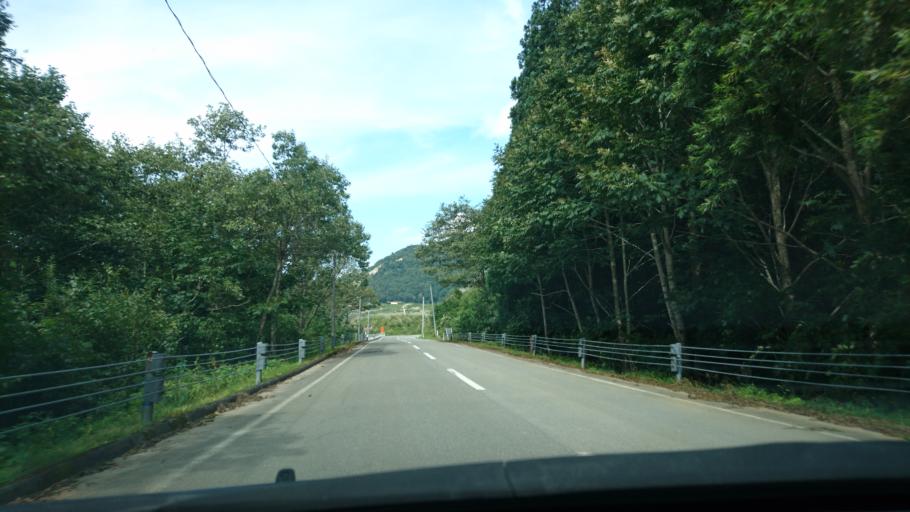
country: JP
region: Akita
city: Yuzawa
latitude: 39.0291
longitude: 140.7278
